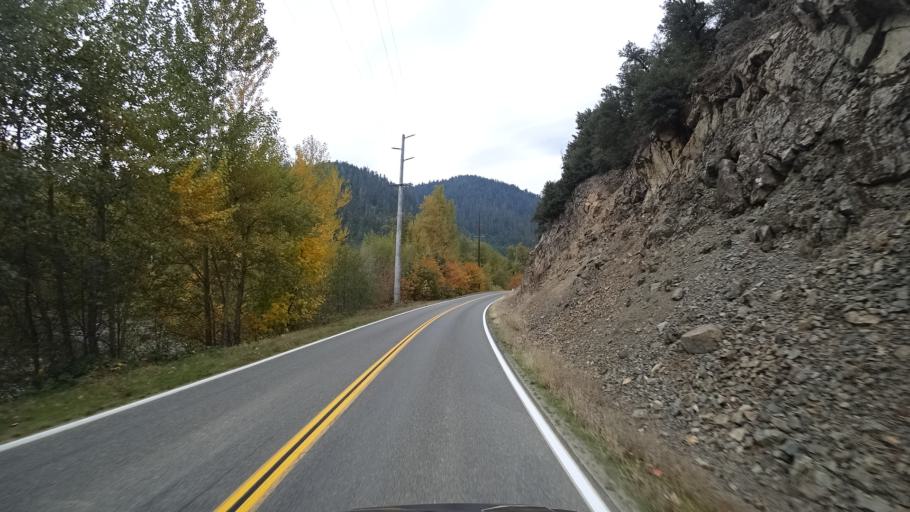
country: US
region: California
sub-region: Siskiyou County
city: Happy Camp
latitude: 41.8831
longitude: -123.4301
